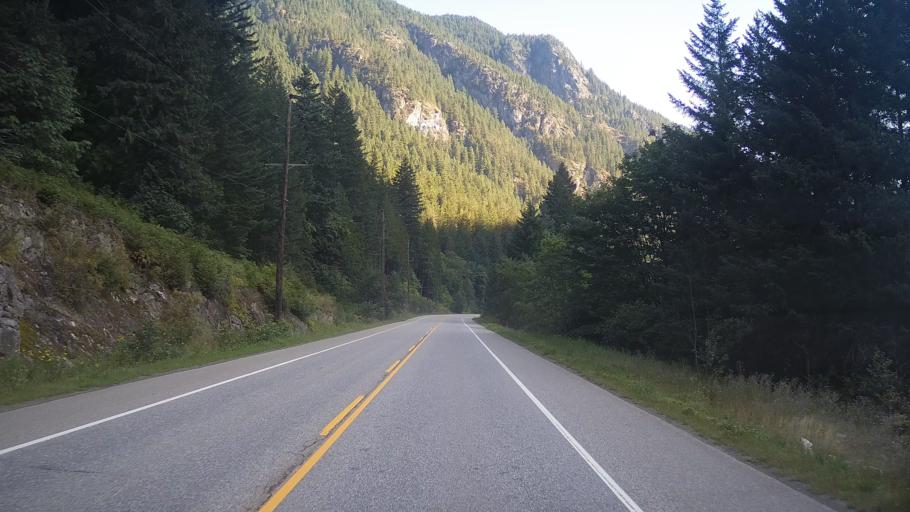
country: CA
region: British Columbia
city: Hope
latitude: 49.6070
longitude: -121.4154
